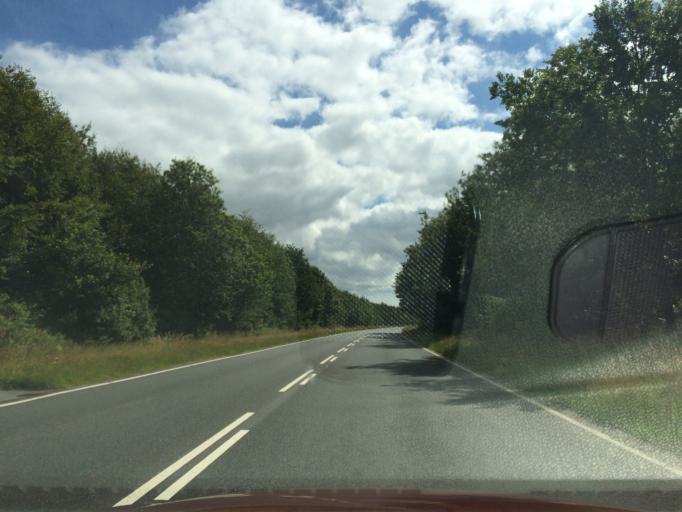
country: DK
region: Central Jutland
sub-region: Silkeborg Kommune
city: Silkeborg
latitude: 56.1946
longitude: 9.6031
